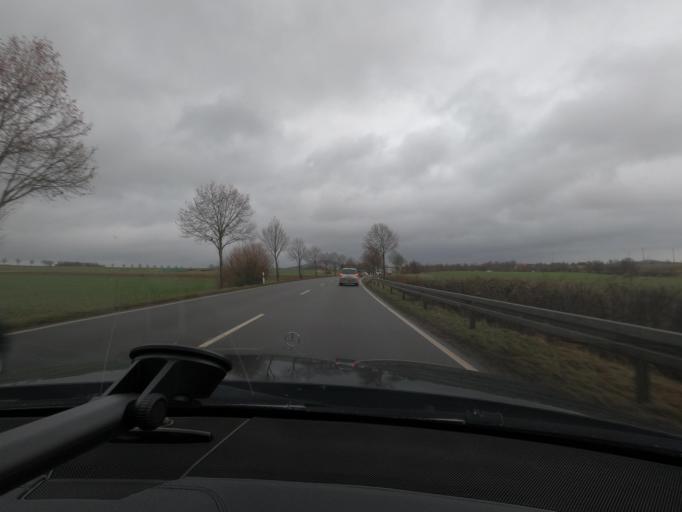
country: DE
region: Hesse
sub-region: Regierungsbezirk Kassel
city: Wolfhagen
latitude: 51.3081
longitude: 9.2137
